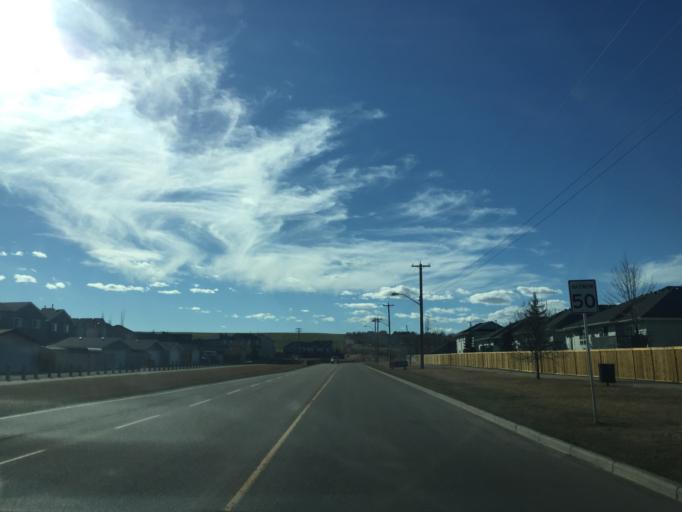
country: CA
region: Alberta
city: Airdrie
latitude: 51.2927
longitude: -114.0429
